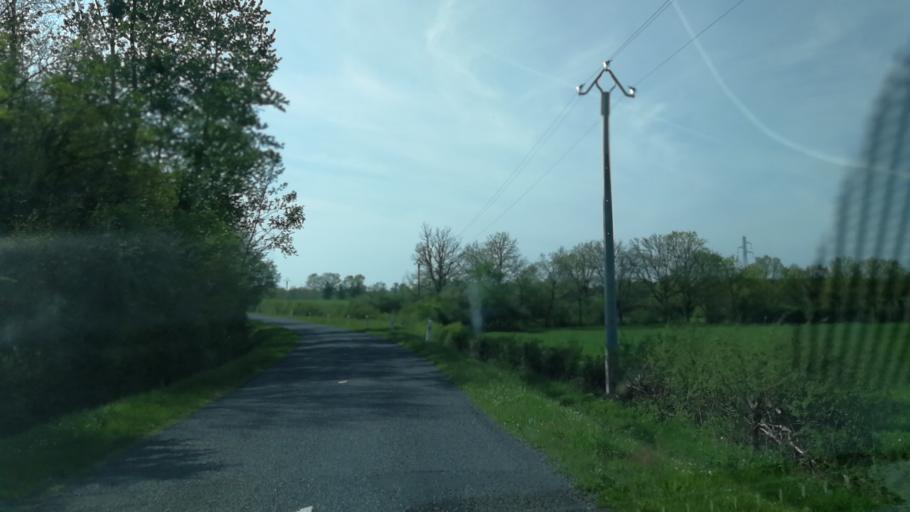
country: FR
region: Auvergne
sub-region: Departement de l'Allier
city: Neuilly-le-Real
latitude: 46.5053
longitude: 3.4827
